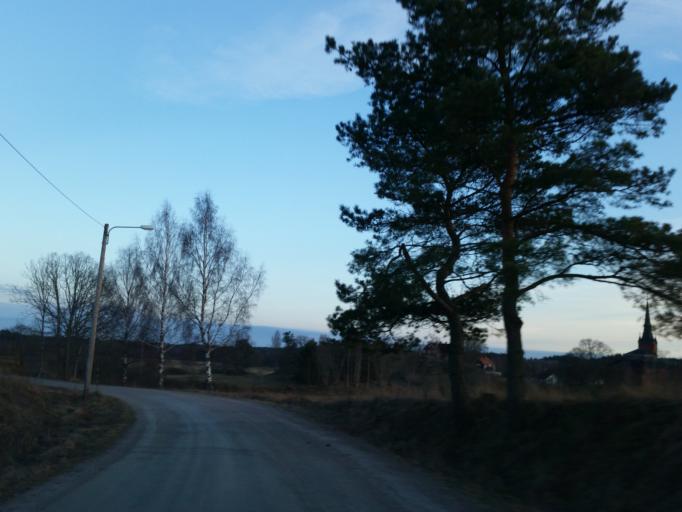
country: SE
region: Kalmar
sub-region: Vasterviks Kommun
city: Ankarsrum
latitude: 57.7129
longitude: 16.4520
